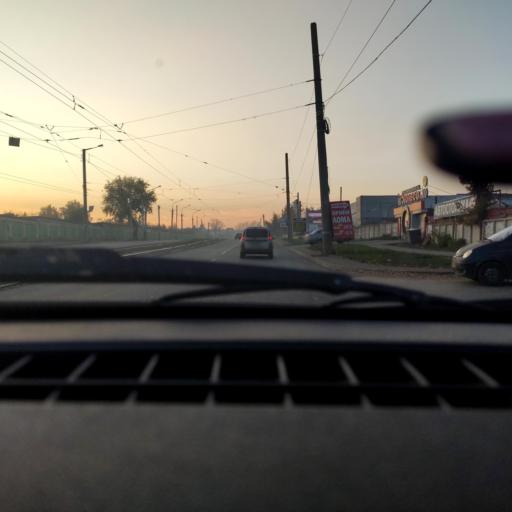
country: RU
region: Bashkortostan
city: Ufa
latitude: 54.8235
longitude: 56.1007
